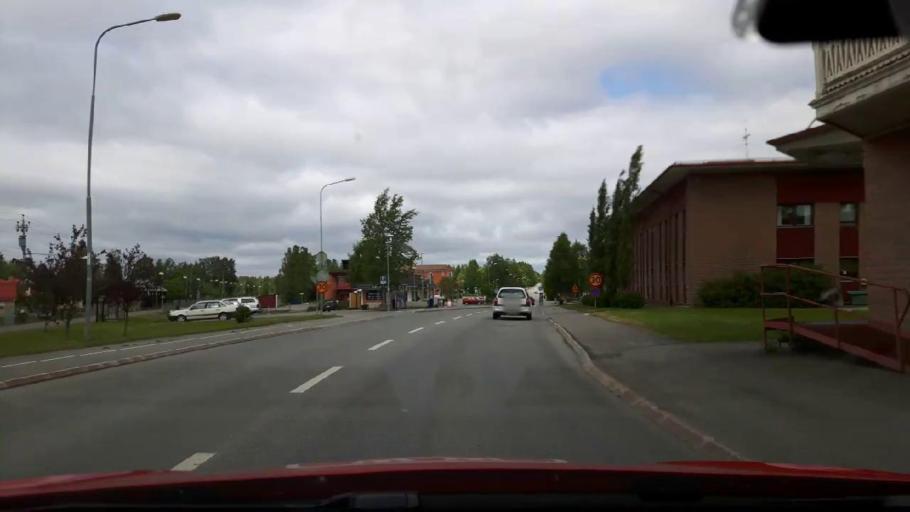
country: SE
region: Jaemtland
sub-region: Krokoms Kommun
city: Krokom
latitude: 63.3257
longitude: 14.4490
